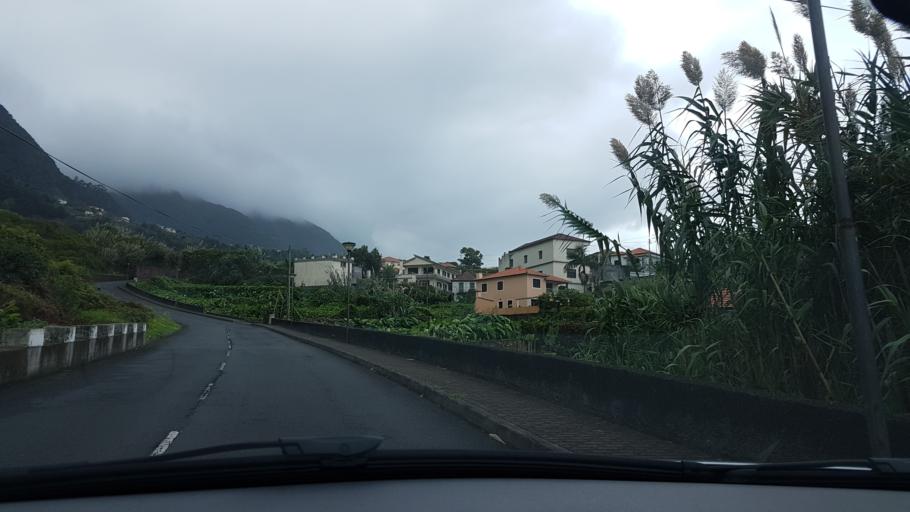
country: PT
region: Madeira
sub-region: Sao Vicente
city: Sao Vicente
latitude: 32.8259
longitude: -16.9865
